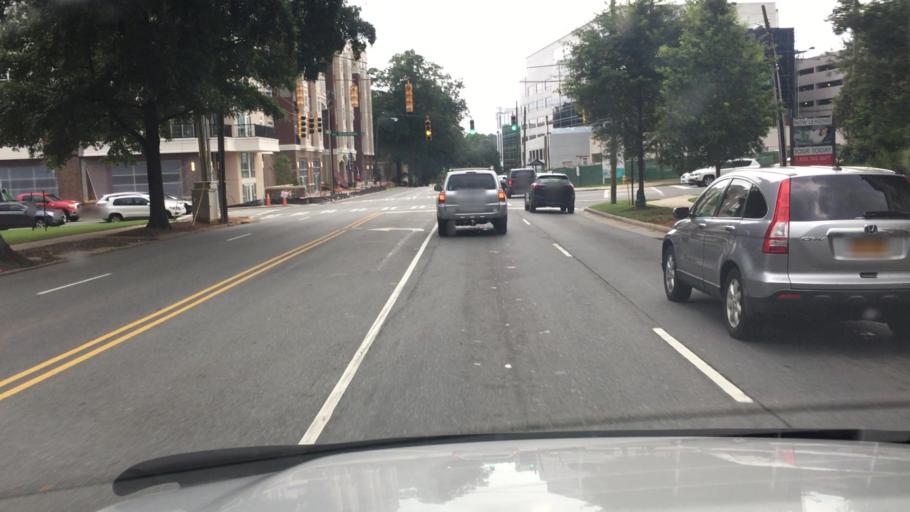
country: US
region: North Carolina
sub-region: Mecklenburg County
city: Charlotte
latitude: 35.2088
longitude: -80.8400
